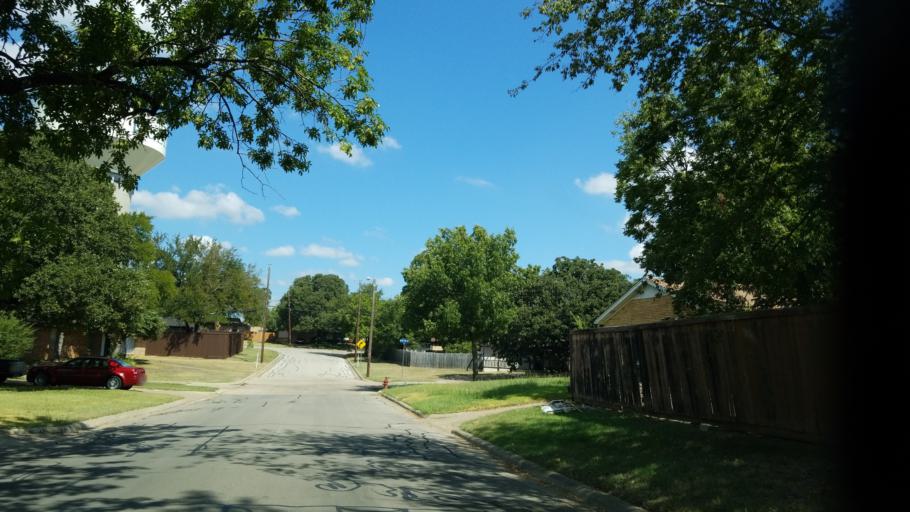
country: US
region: Texas
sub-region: Tarrant County
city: Euless
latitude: 32.8337
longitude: -97.0778
